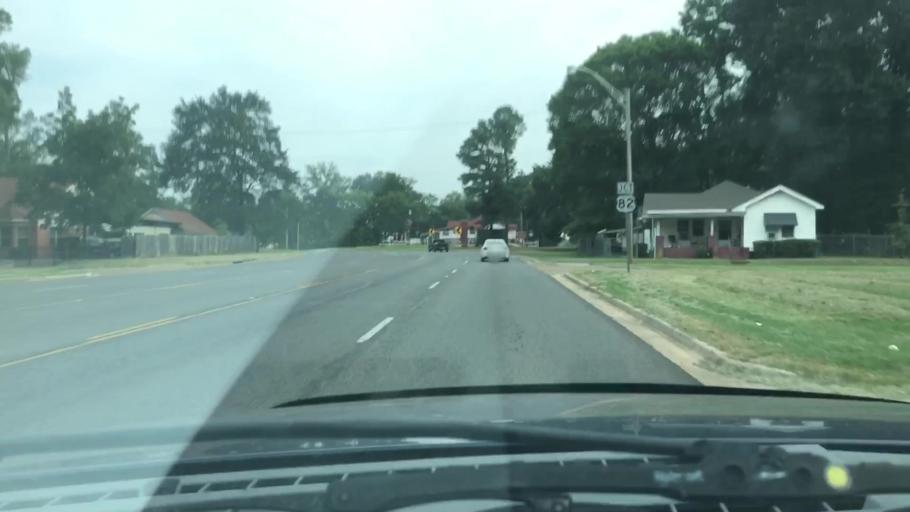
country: US
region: Texas
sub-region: Bowie County
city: Texarkana
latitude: 33.4315
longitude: -94.0616
